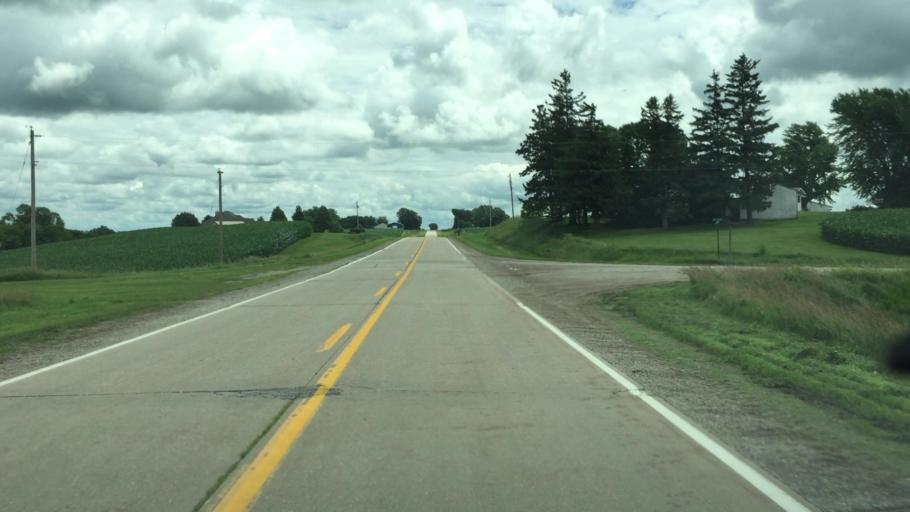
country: US
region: Iowa
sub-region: Jasper County
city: Monroe
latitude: 41.5807
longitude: -93.1213
